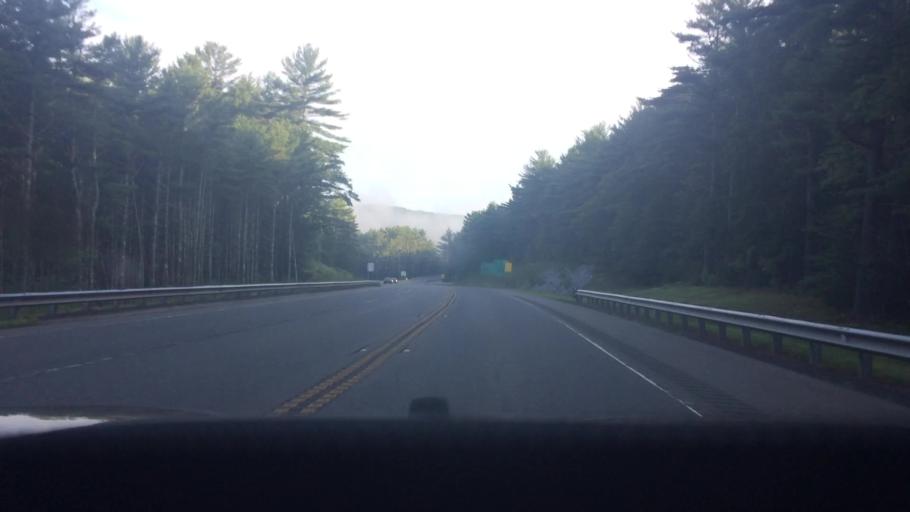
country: US
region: Massachusetts
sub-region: Franklin County
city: Orange
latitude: 42.5861
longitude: -72.3269
